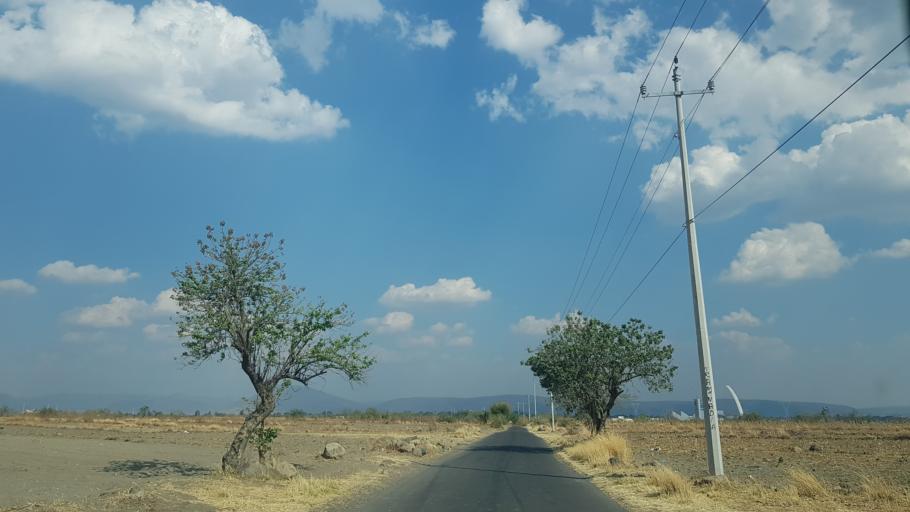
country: MX
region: Puebla
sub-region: Atlixco
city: Colonia Agricola de Ocotepec (Colonia San Jose)
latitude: 18.8907
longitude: -98.5051
